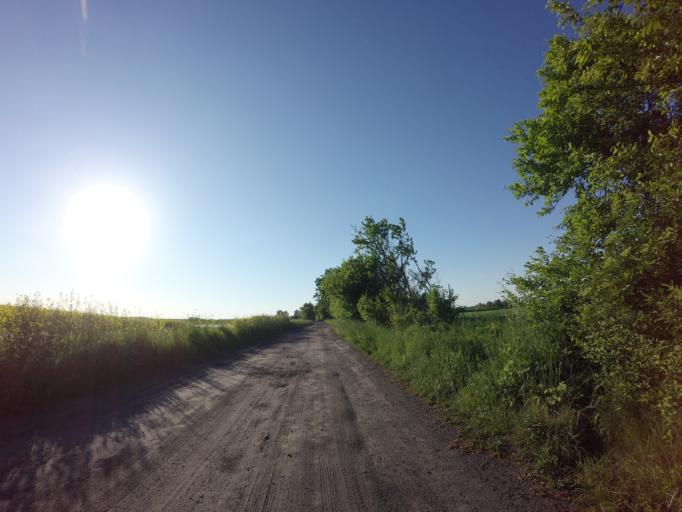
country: PL
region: West Pomeranian Voivodeship
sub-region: Powiat choszczenski
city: Choszczno
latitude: 53.1384
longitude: 15.4349
